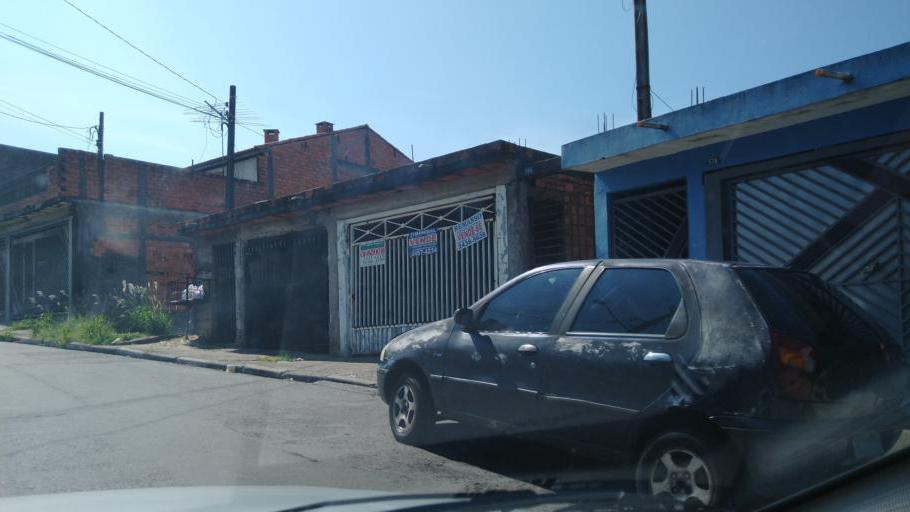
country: BR
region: Sao Paulo
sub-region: Aruja
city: Aruja
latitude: -23.4156
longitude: -46.4030
